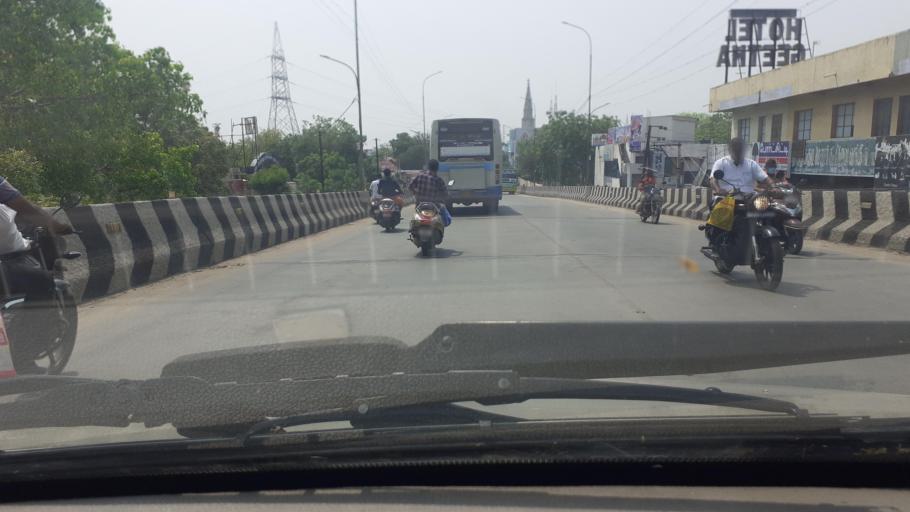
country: IN
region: Tamil Nadu
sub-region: Thoothukkudi
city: Korampallam
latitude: 8.8103
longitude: 78.1387
